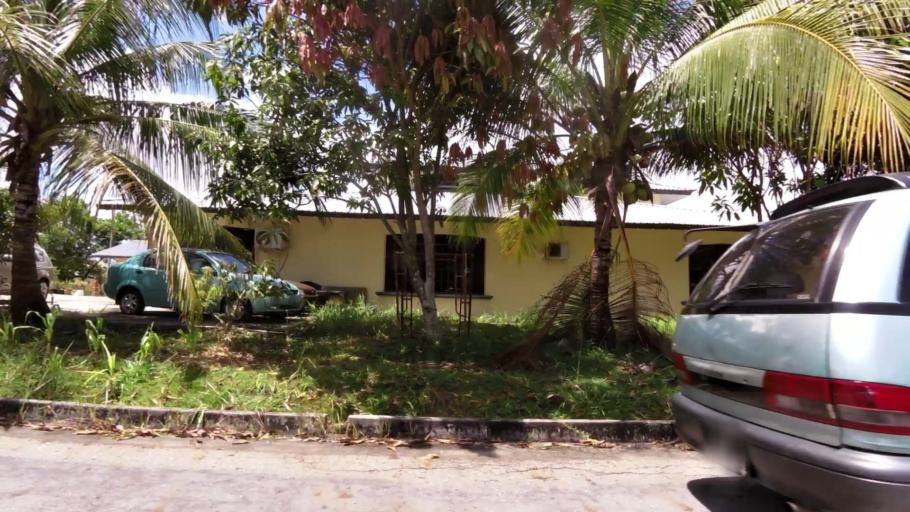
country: BN
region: Brunei and Muara
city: Bandar Seri Begawan
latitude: 4.9607
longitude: 114.9130
